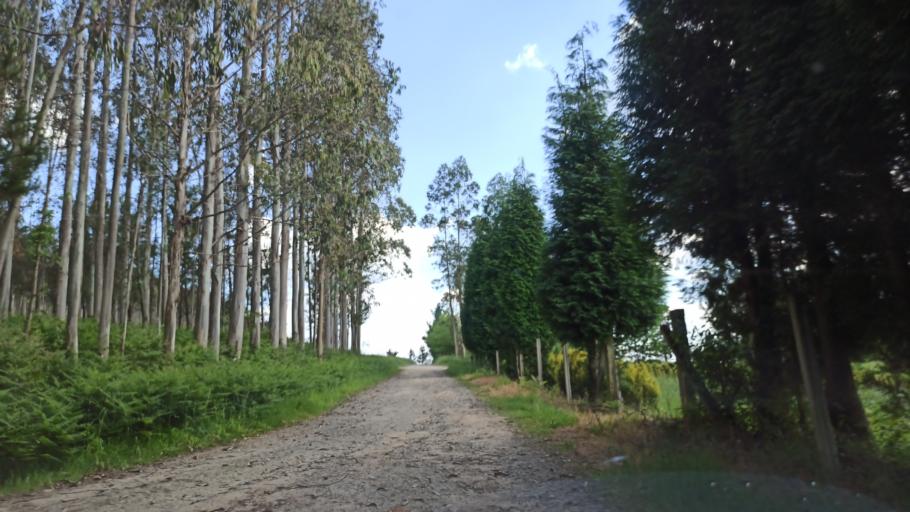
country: ES
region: Galicia
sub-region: Provincia da Coruna
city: Santa Comba
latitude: 43.0763
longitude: -8.7170
